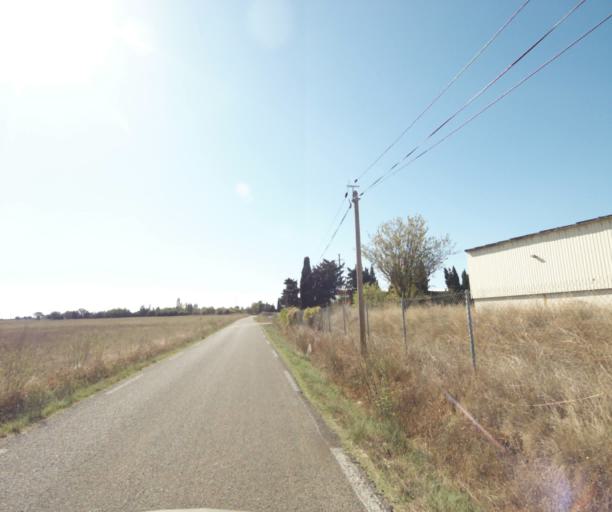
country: FR
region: Languedoc-Roussillon
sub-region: Departement du Gard
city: Rodilhan
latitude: 43.8176
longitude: 4.4286
